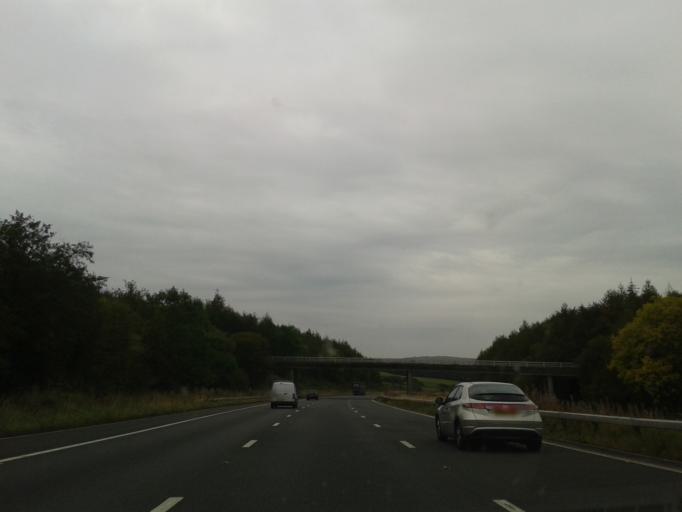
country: GB
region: England
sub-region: Cumbria
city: Kendal
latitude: 54.2633
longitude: -2.6845
